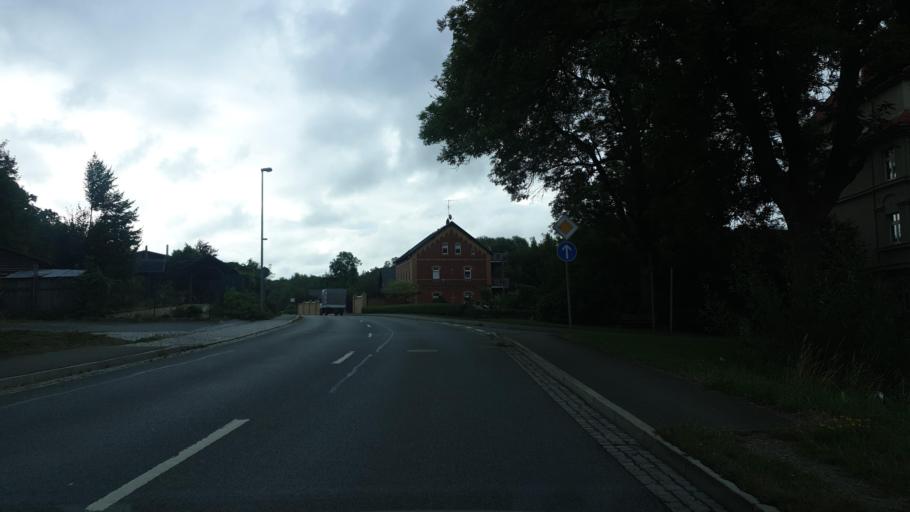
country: DE
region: Saxony
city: Mylau
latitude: 50.6202
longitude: 12.2672
